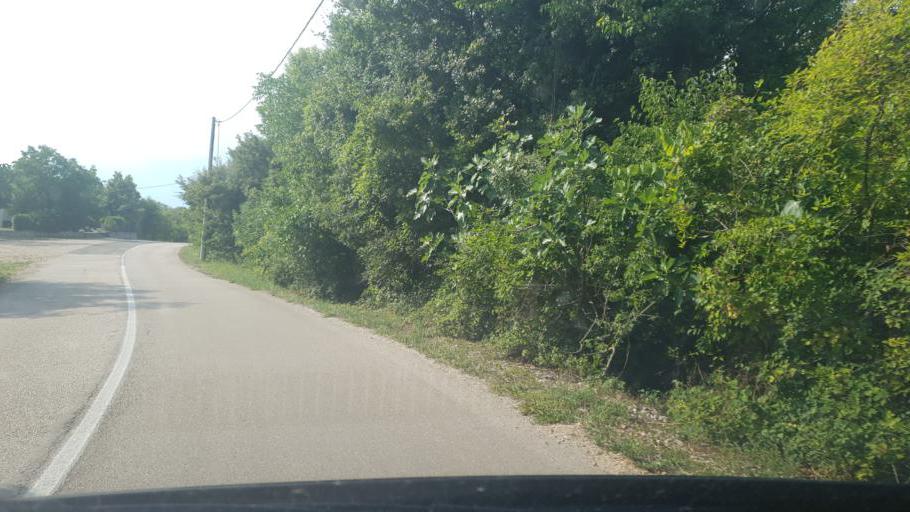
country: HR
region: Primorsko-Goranska
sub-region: Grad Crikvenica
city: Crikvenica
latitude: 45.1369
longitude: 14.6217
